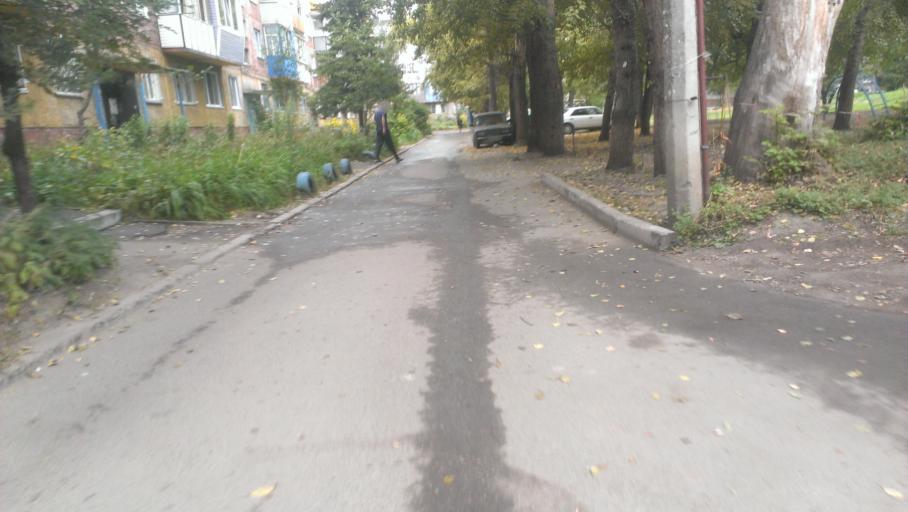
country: RU
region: Altai Krai
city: Novosilikatnyy
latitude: 53.3736
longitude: 83.6711
